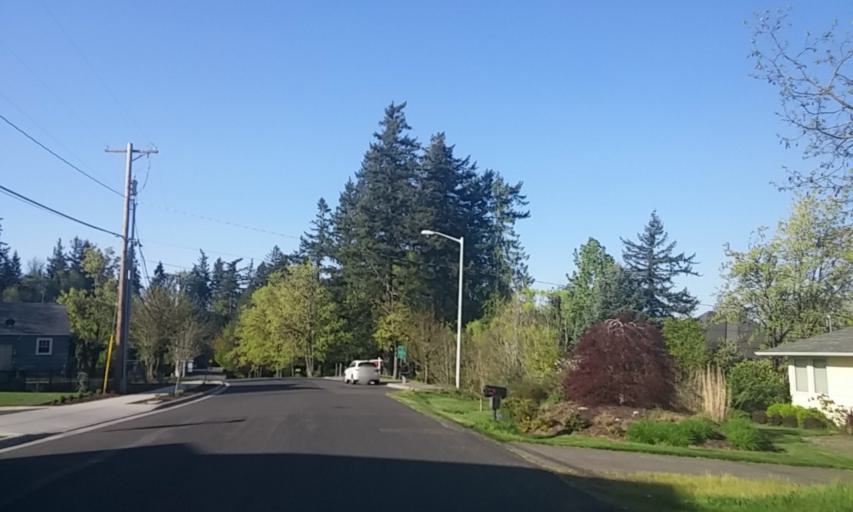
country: US
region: Oregon
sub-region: Washington County
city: Cedar Mill
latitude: 45.5462
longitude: -122.7925
